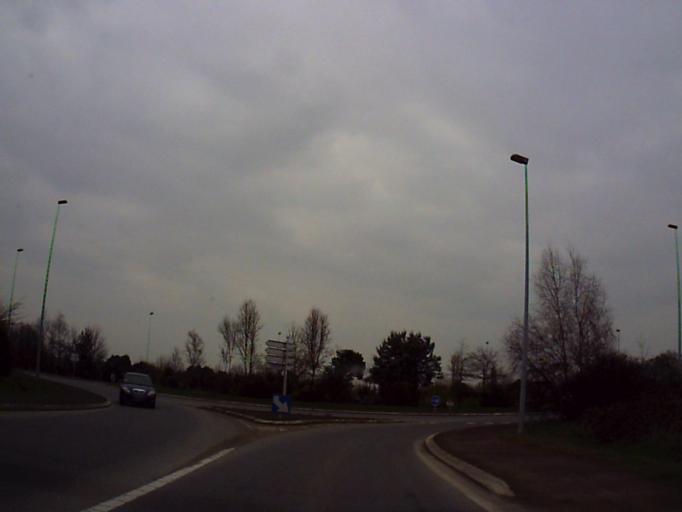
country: FR
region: Brittany
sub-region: Departement d'Ille-et-Vilaine
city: Saint-Gregoire
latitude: 48.1438
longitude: -1.6570
